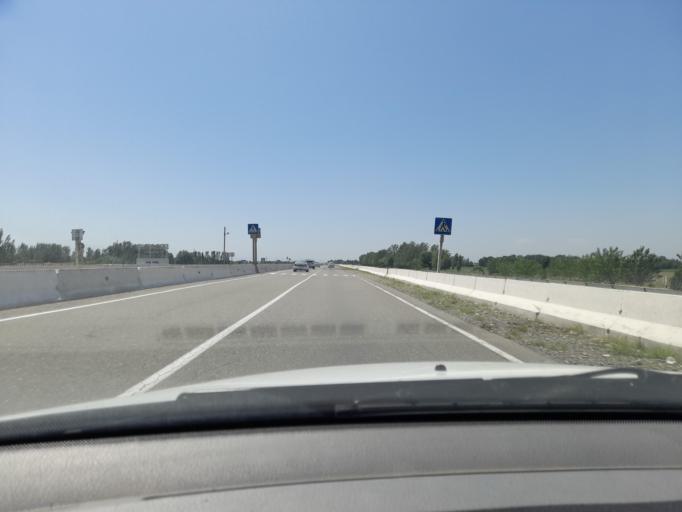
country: UZ
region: Jizzax
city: Paxtakor
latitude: 40.3302
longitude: 68.1068
